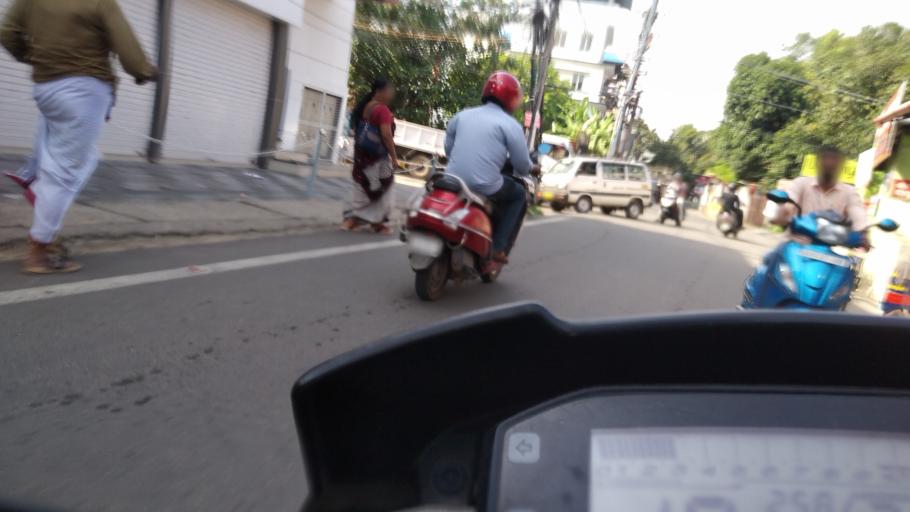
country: IN
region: Kerala
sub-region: Ernakulam
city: Cochin
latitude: 9.9813
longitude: 76.2868
